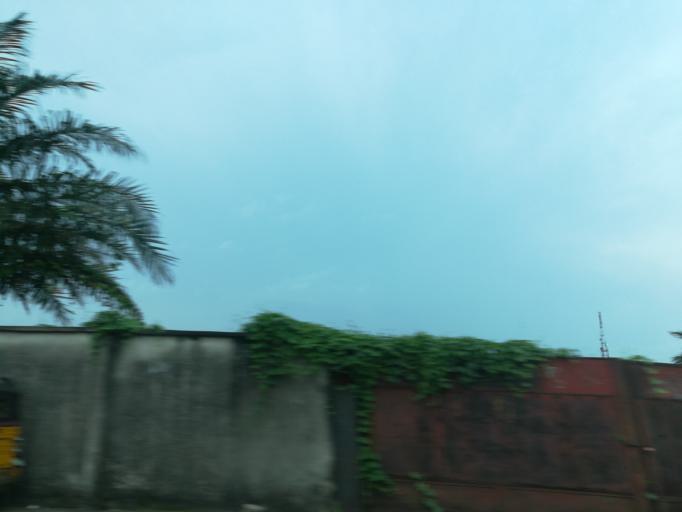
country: NG
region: Rivers
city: Port Harcourt
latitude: 4.7996
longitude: 7.0199
